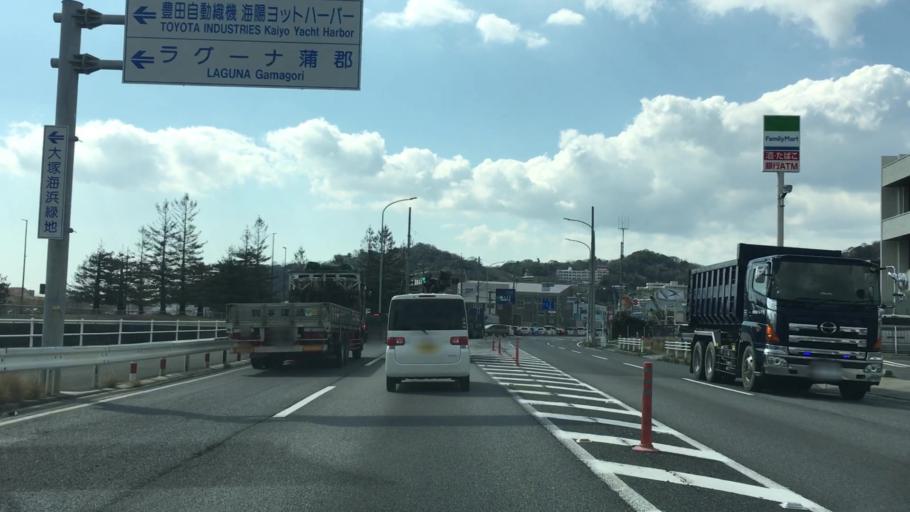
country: JP
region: Aichi
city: Gamagori
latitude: 34.8111
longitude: 137.2750
